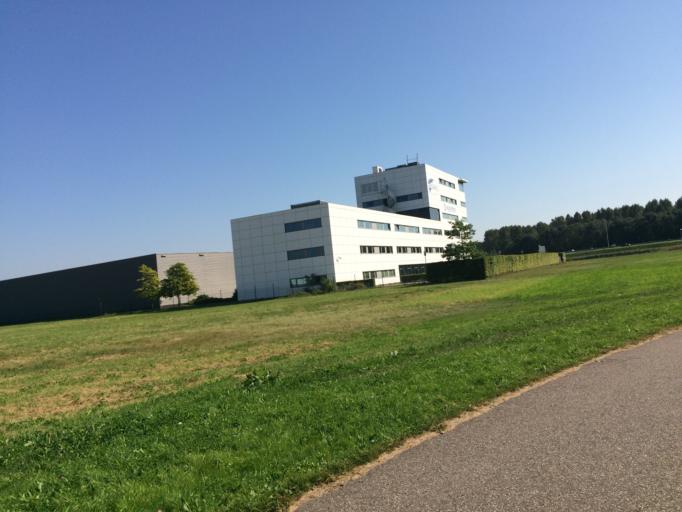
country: NL
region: Flevoland
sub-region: Gemeente Almere
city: Almere Stad
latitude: 52.3553
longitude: 5.2439
